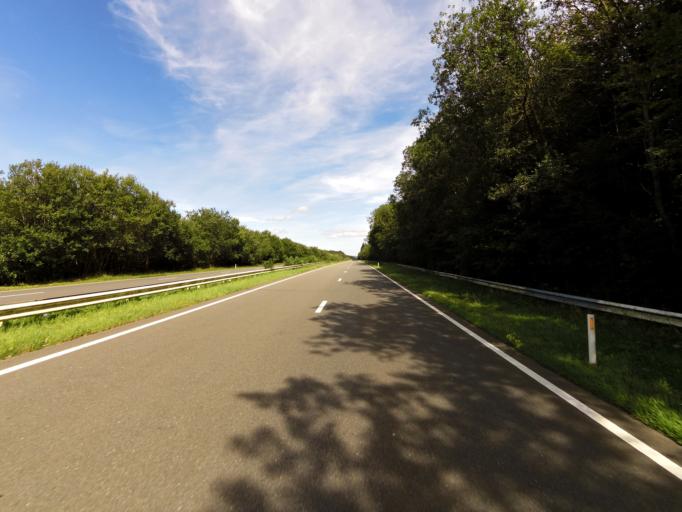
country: BE
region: Wallonia
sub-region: Province du Luxembourg
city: Tenneville
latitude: 50.0933
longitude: 5.4545
